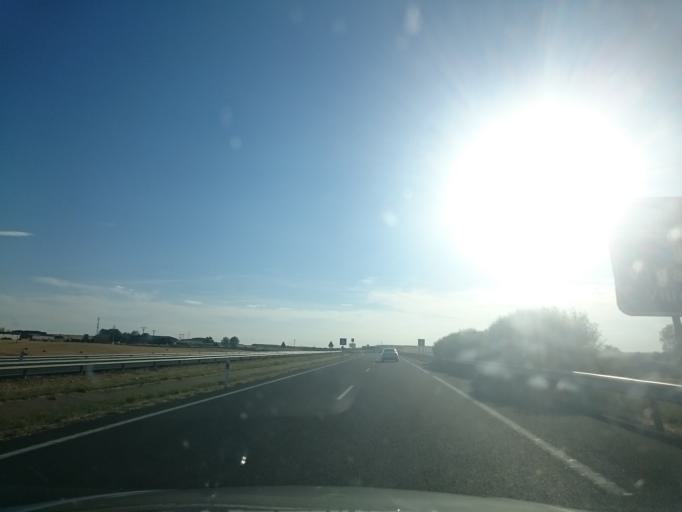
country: ES
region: Castille and Leon
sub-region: Provincia de Palencia
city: Villaherreros
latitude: 42.3928
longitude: -4.4608
